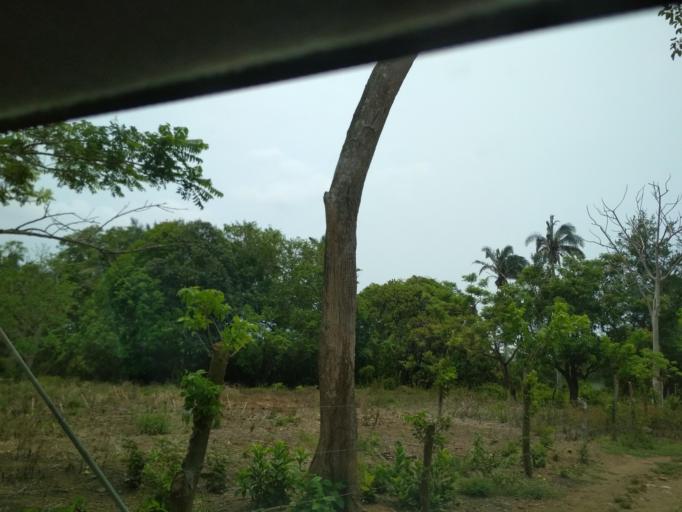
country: MX
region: Veracruz
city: Paso del Toro
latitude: 19.0436
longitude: -96.1639
